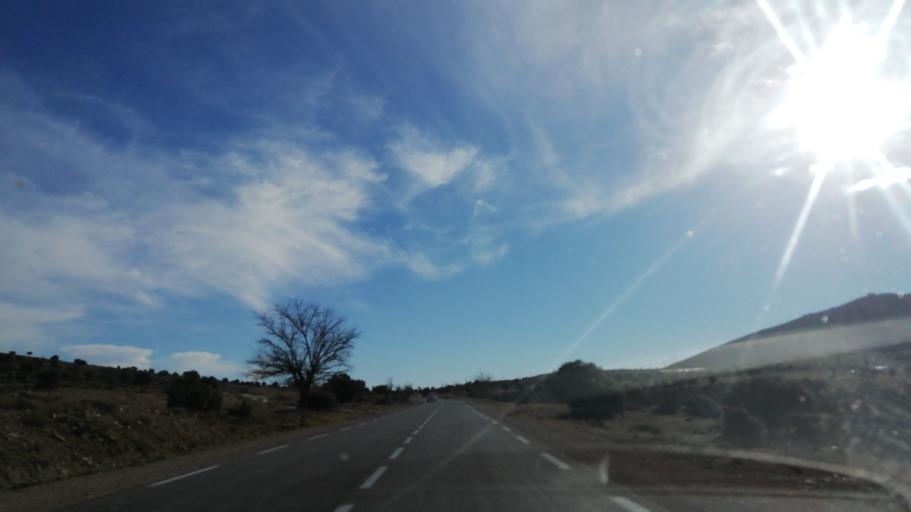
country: DZ
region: Tlemcen
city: Sebdou
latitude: 34.5773
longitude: -1.3196
